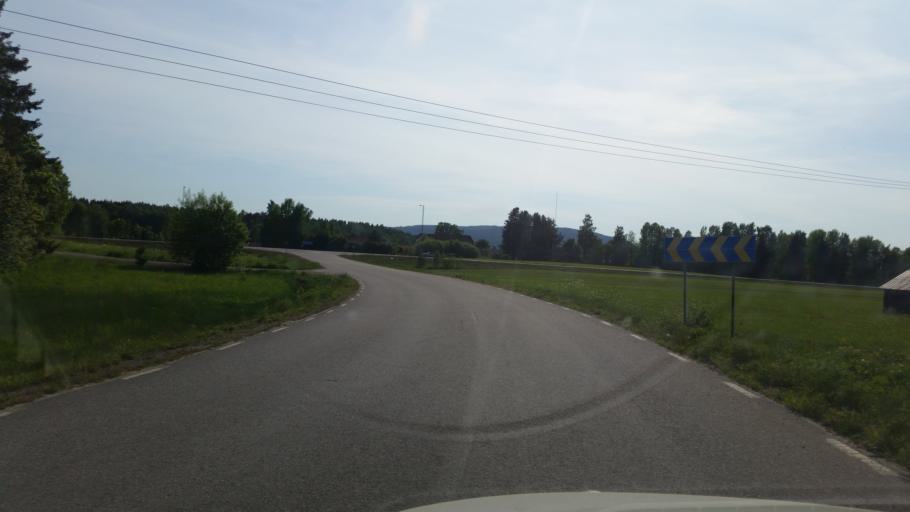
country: SE
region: Gaevleborg
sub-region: Hudiksvalls Kommun
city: Sorforsa
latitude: 61.7309
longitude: 16.9658
